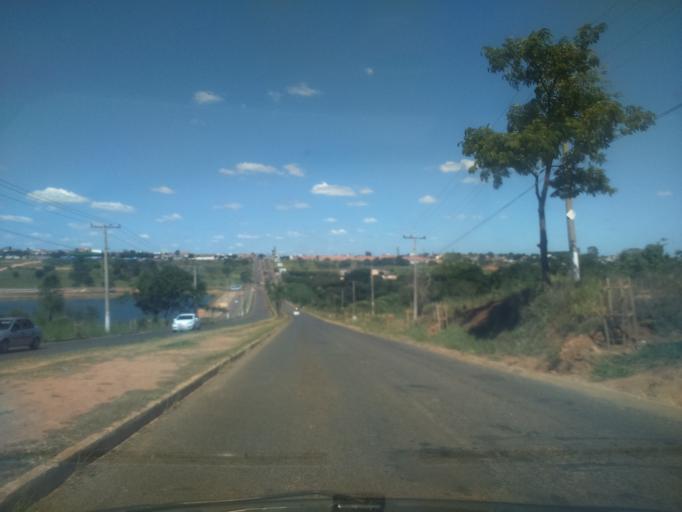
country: BR
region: Goias
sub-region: Luziania
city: Luziania
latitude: -16.1093
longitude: -47.9428
